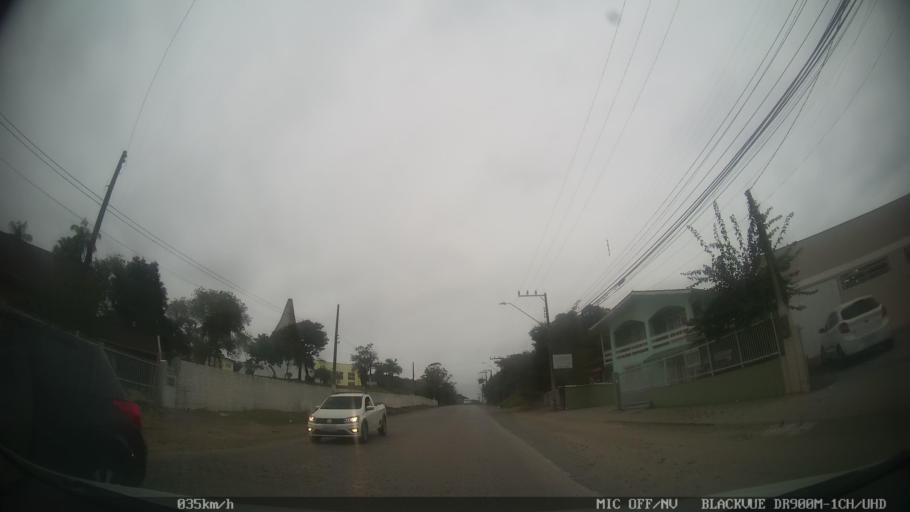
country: BR
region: Santa Catarina
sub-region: Joinville
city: Joinville
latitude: -26.3575
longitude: -48.8451
